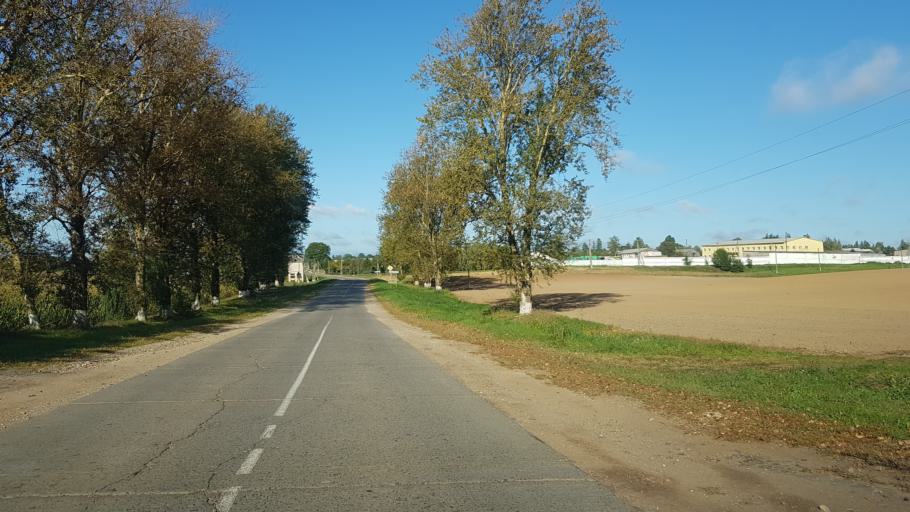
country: BY
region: Minsk
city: Dzyarzhynsk
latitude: 53.7354
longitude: 27.2178
